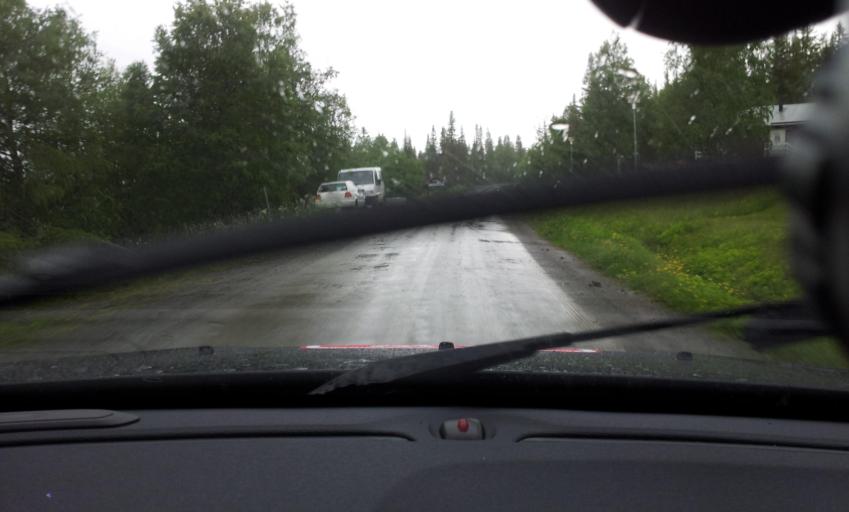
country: SE
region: Jaemtland
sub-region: Are Kommun
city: Are
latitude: 63.2184
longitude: 13.0616
